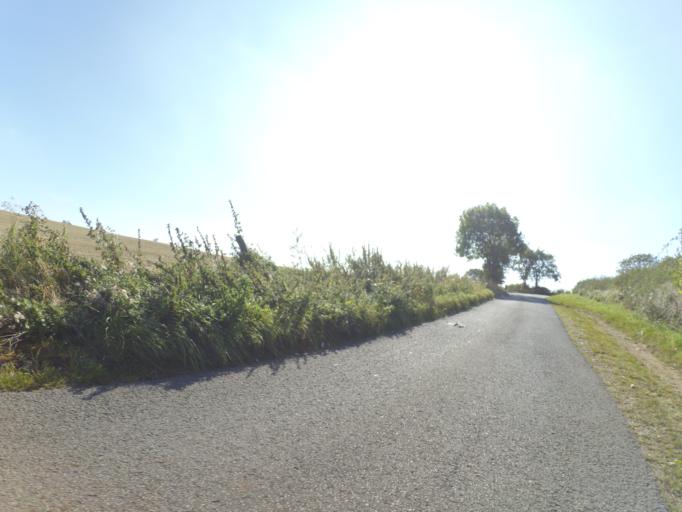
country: GB
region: England
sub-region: Warwickshire
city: Rugby
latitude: 52.4163
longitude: -1.2568
